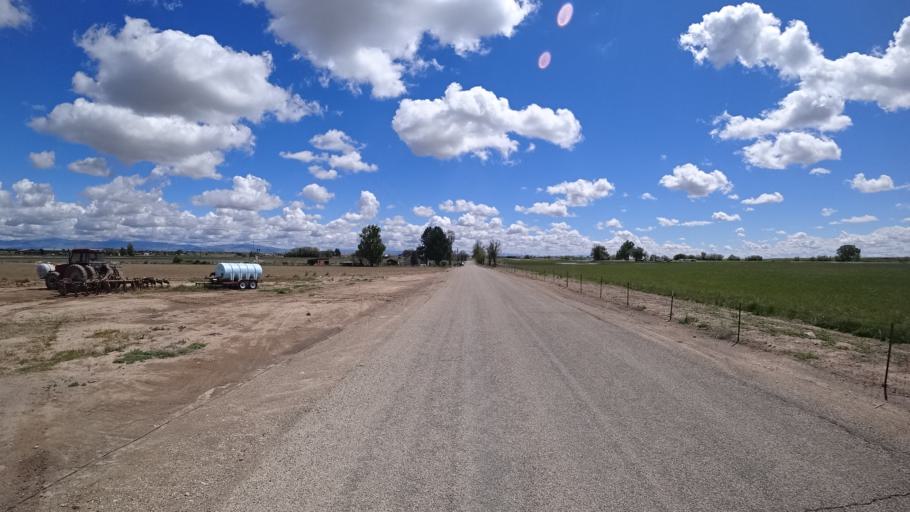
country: US
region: Idaho
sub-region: Ada County
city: Kuna
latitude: 43.4592
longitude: -116.3608
